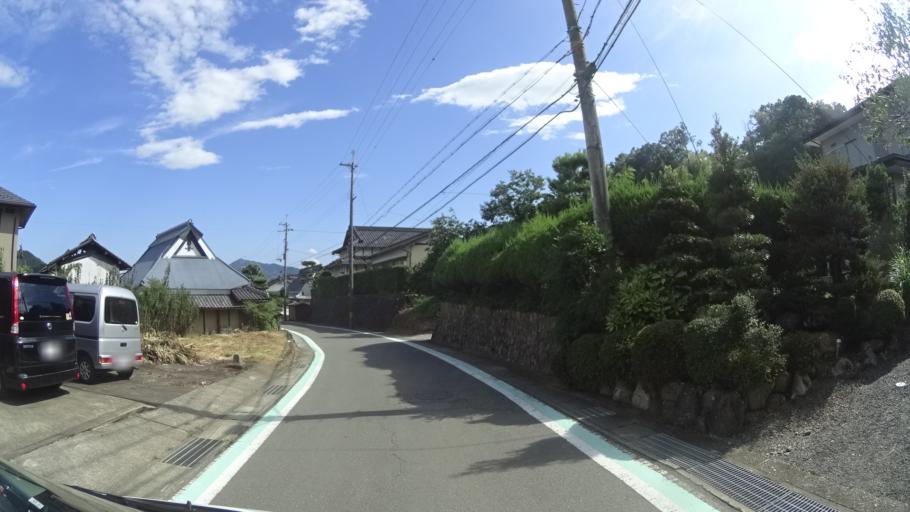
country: JP
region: Kyoto
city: Fukuchiyama
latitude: 35.3254
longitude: 135.1768
